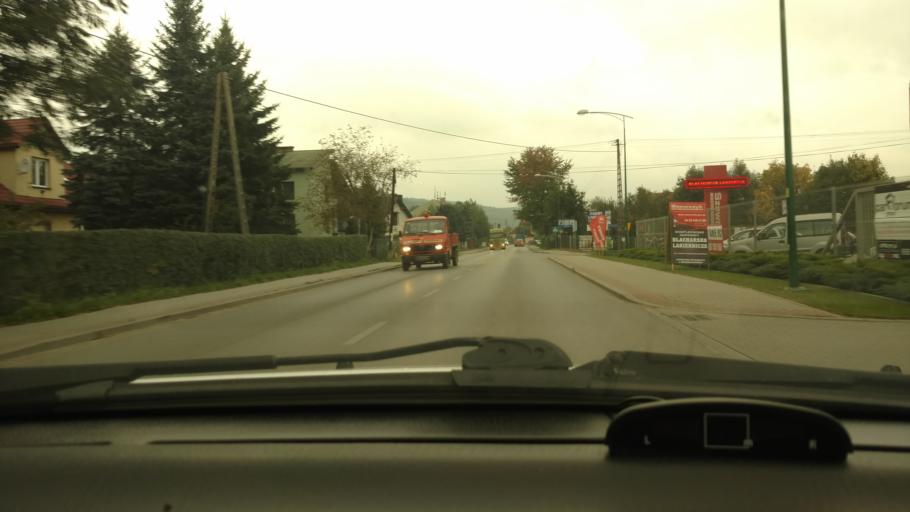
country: PL
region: Lesser Poland Voivodeship
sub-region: Powiat nowosadecki
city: Chelmiec
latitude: 49.6281
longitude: 20.6677
